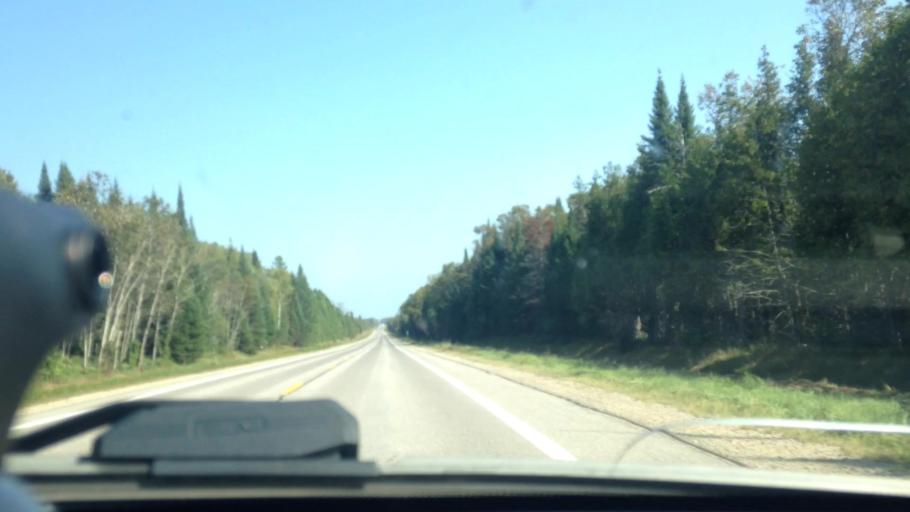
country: US
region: Michigan
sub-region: Luce County
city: Newberry
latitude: 46.3036
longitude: -85.4117
